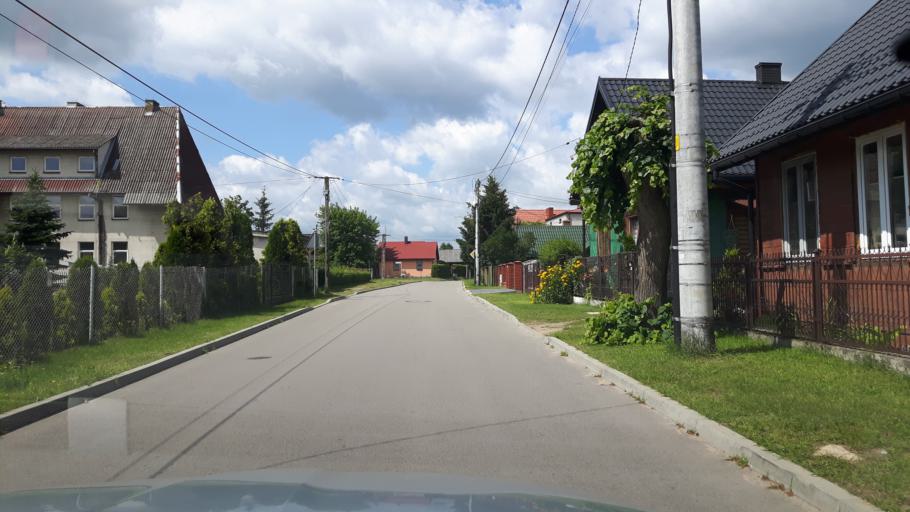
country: PL
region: Masovian Voivodeship
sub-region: Powiat ostrowski
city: Brok
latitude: 52.6996
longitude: 21.8588
